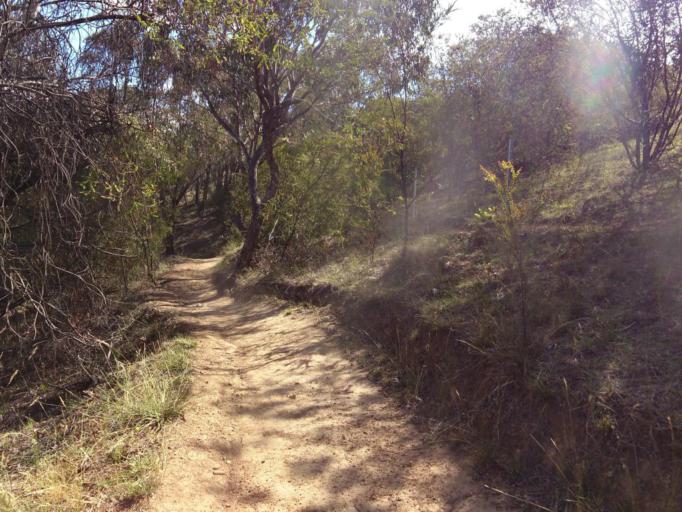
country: AU
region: Australian Capital Territory
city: Belconnen
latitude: -35.1506
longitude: 149.0880
